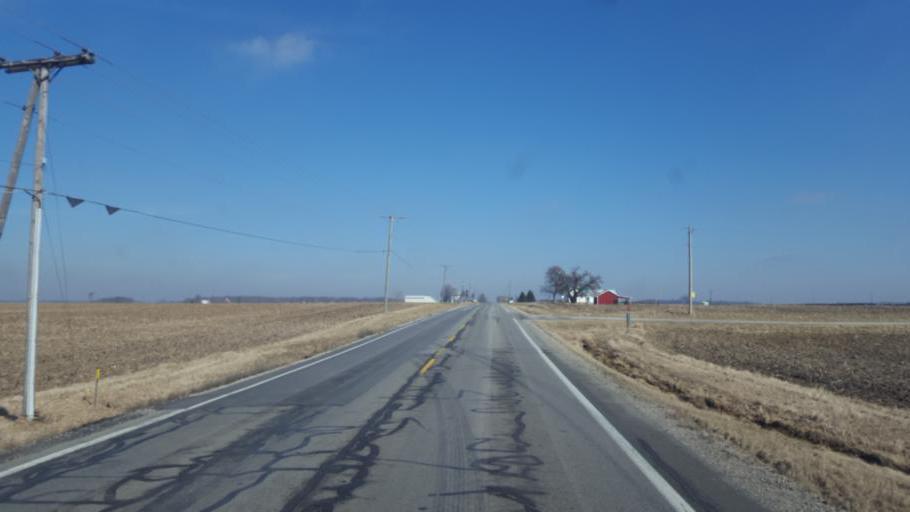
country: US
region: Ohio
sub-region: Huron County
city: Willard
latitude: 41.0266
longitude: -82.9066
